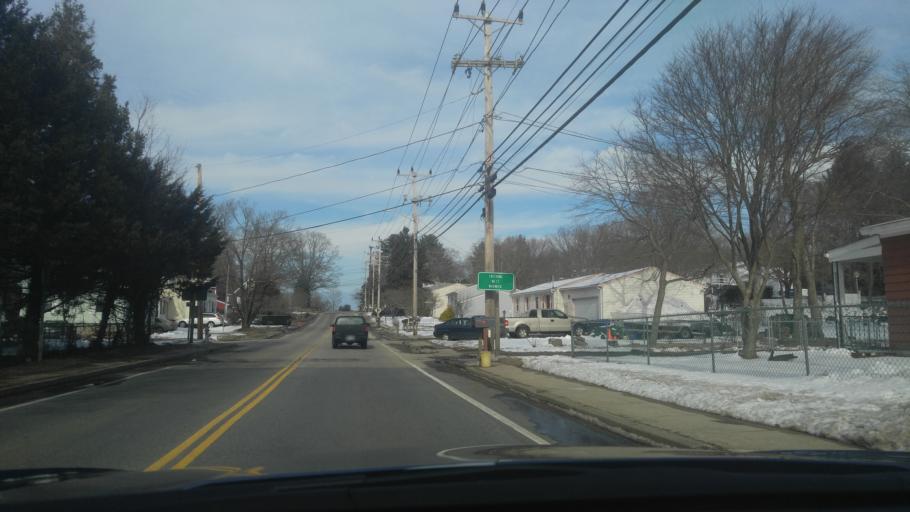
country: US
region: Rhode Island
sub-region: Kent County
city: West Warwick
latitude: 41.6709
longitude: -71.5335
